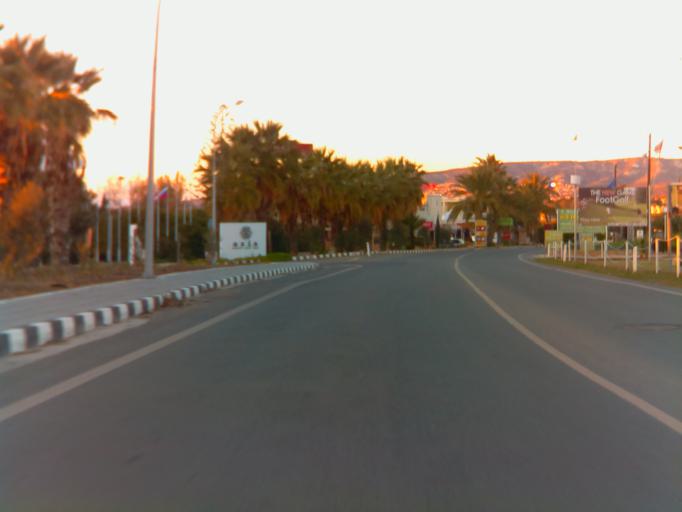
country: CY
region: Pafos
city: Kissonerga
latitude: 34.8090
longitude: 32.3963
